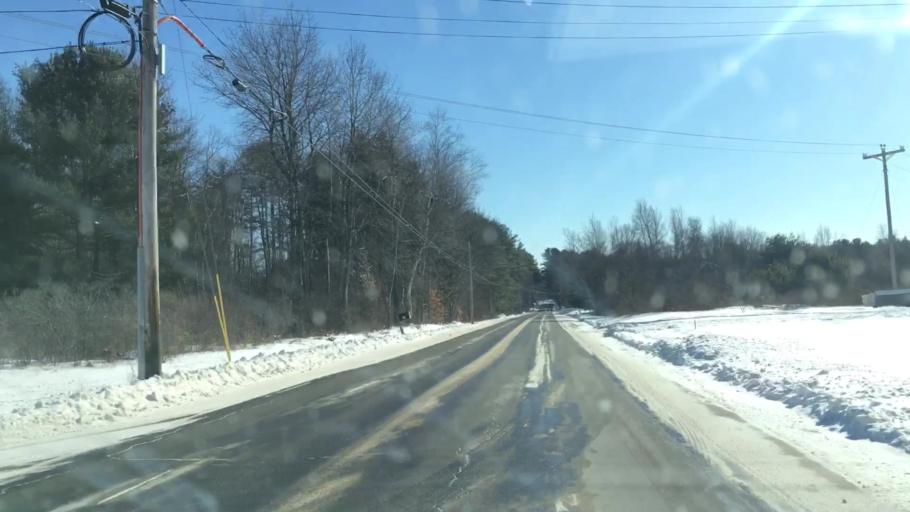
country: US
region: Maine
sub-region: Sagadahoc County
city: Topsham
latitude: 43.9058
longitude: -70.0036
